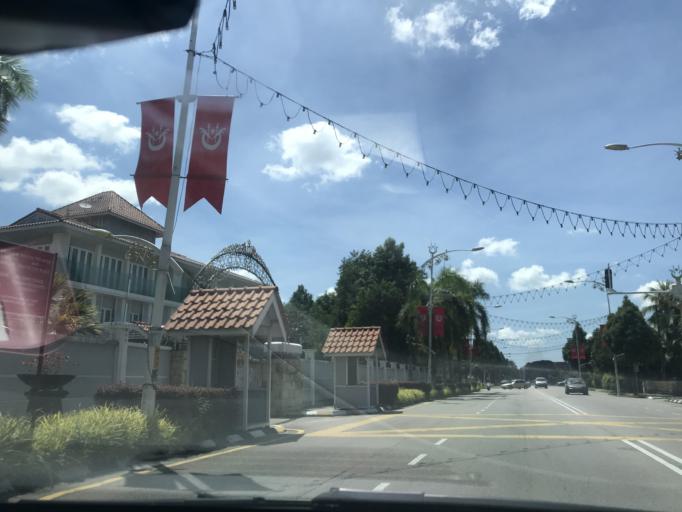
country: MY
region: Kelantan
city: Kota Bharu
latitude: 6.1088
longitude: 102.2459
